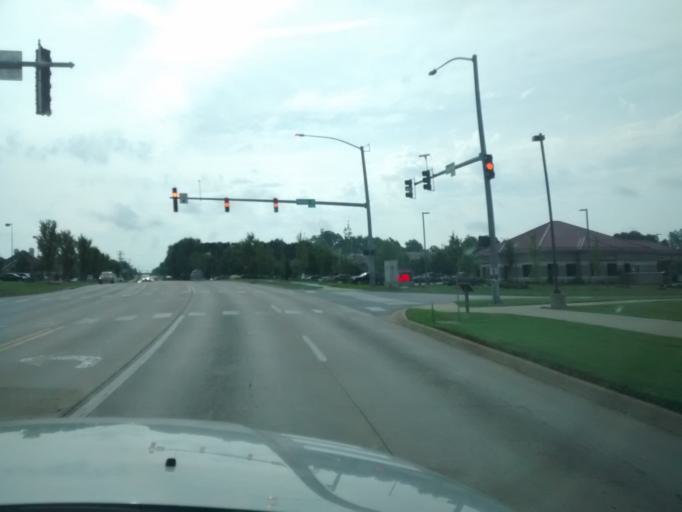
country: US
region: Arkansas
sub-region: Washington County
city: Johnson
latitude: 36.1202
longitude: -94.1387
